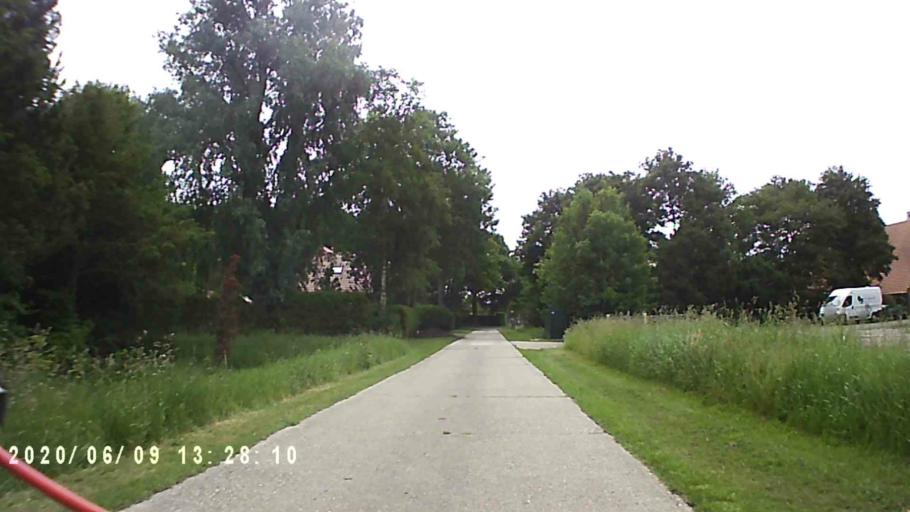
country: NL
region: Groningen
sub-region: Gemeente Haren
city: Haren
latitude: 53.2130
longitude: 6.6821
